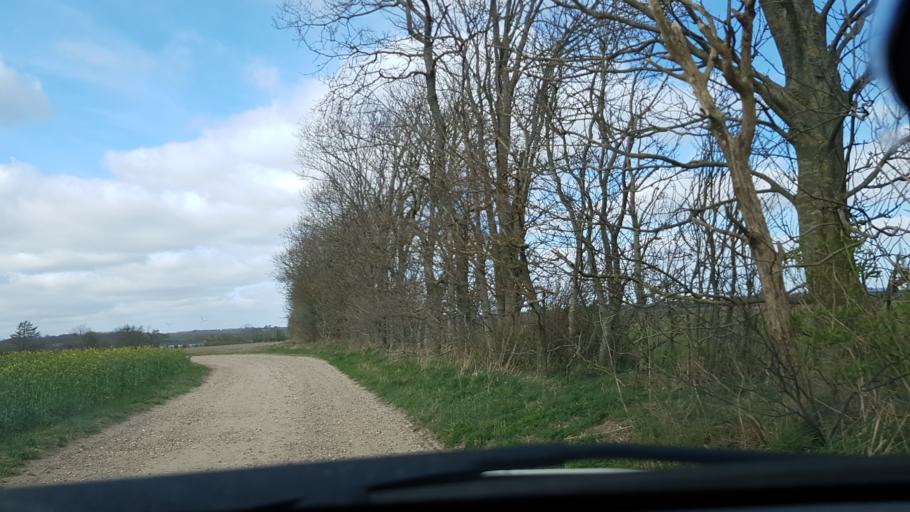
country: DK
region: South Denmark
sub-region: Vejen Kommune
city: Rodding
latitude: 55.3713
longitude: 8.9664
